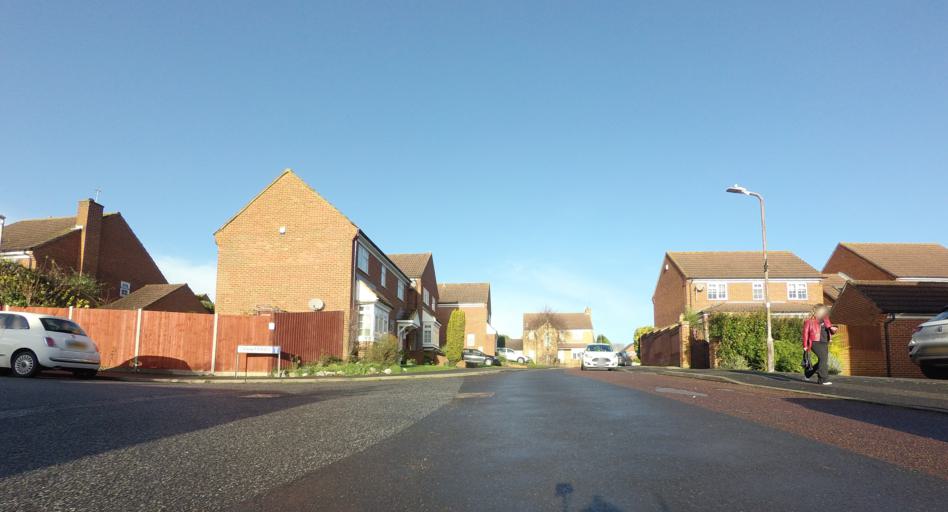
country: GB
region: England
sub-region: Kent
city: Swanley
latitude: 51.4098
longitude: 0.1767
